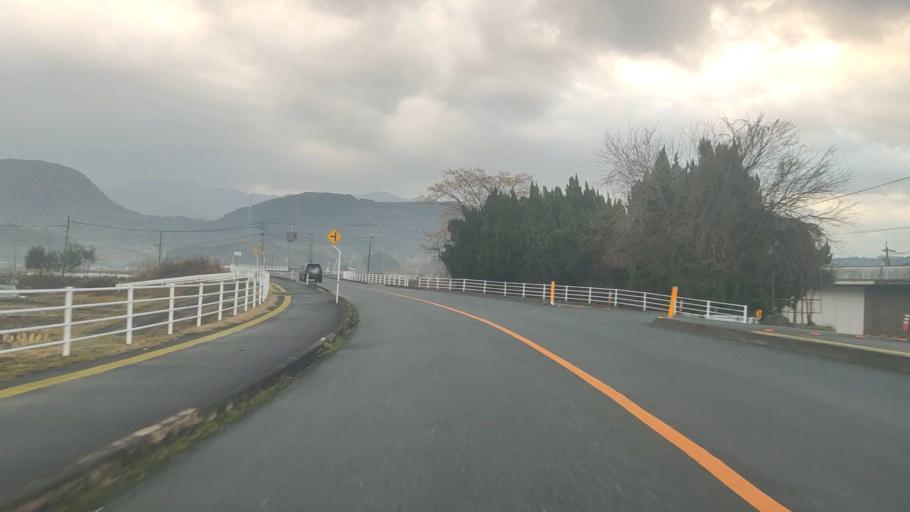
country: JP
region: Kumamoto
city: Matsubase
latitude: 32.6449
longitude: 130.8119
